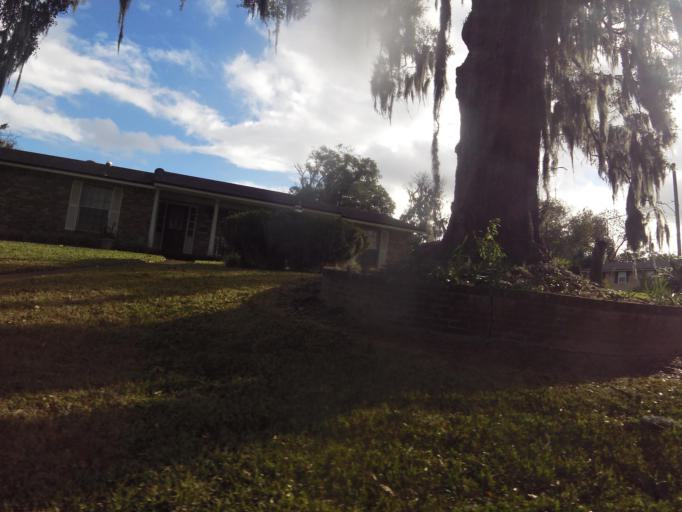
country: US
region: Florida
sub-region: Duval County
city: Jacksonville
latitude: 30.3379
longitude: -81.5798
